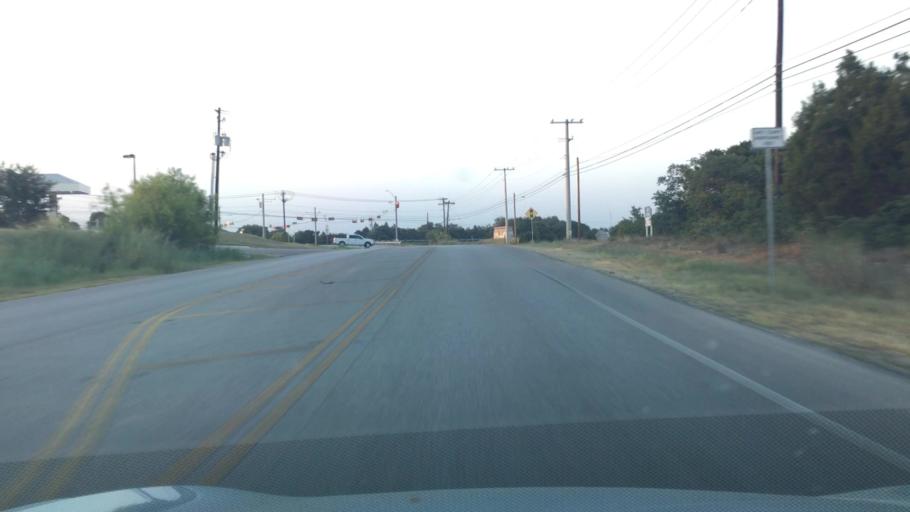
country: US
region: Texas
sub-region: Hays County
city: Dripping Springs
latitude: 30.1950
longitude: -97.9978
